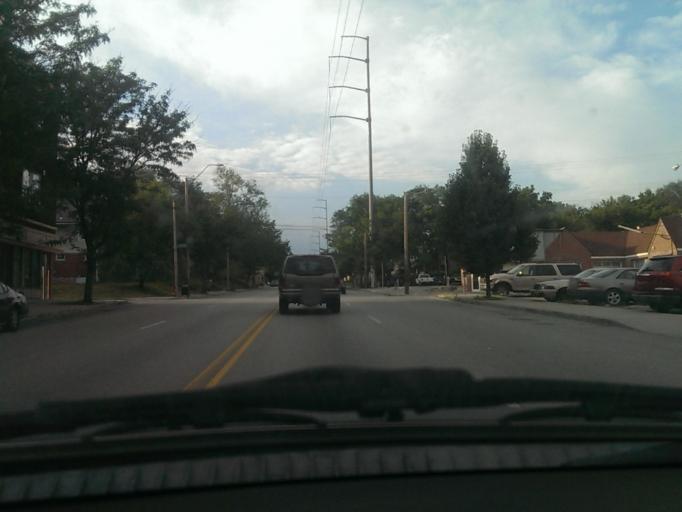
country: US
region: Kansas
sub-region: Johnson County
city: Westwood
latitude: 39.0503
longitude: -94.5724
